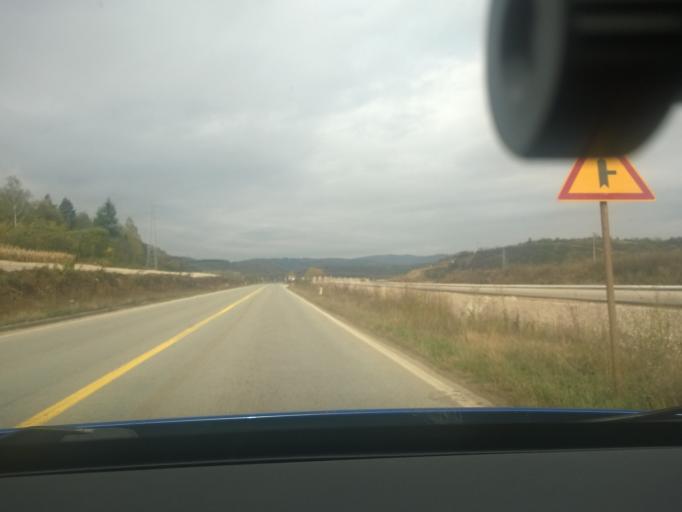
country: RS
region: Central Serbia
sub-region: Pirotski Okrug
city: Pirot
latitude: 43.2077
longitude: 22.5524
